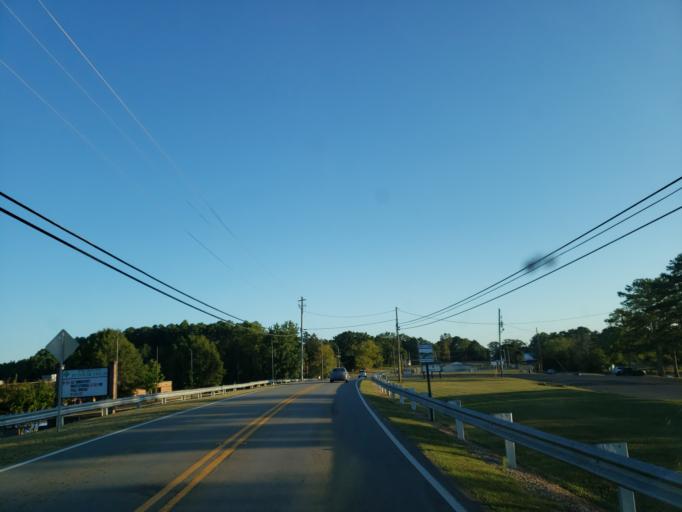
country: US
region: Georgia
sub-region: Pickens County
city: Jasper
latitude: 34.4444
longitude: -84.4211
